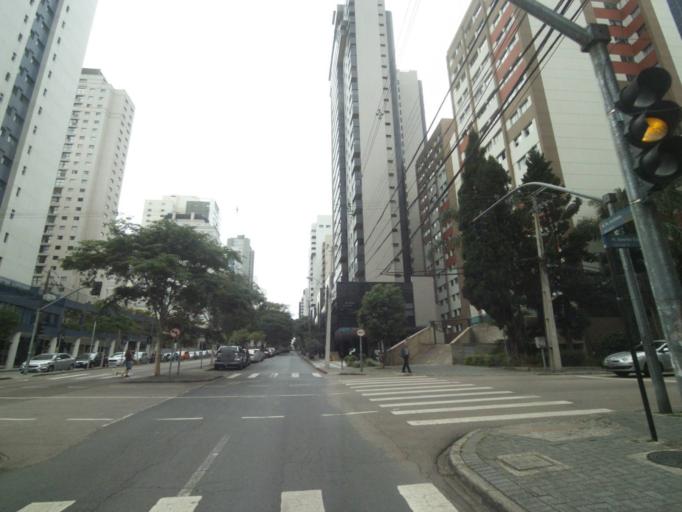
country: BR
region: Parana
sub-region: Curitiba
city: Curitiba
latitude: -25.4347
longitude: -49.3033
